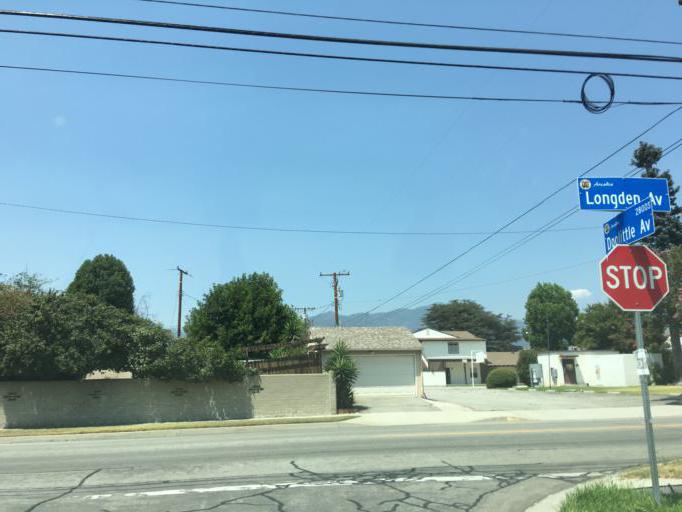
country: US
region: California
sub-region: Los Angeles County
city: Mayflower Village
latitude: 34.1142
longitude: -118.0132
